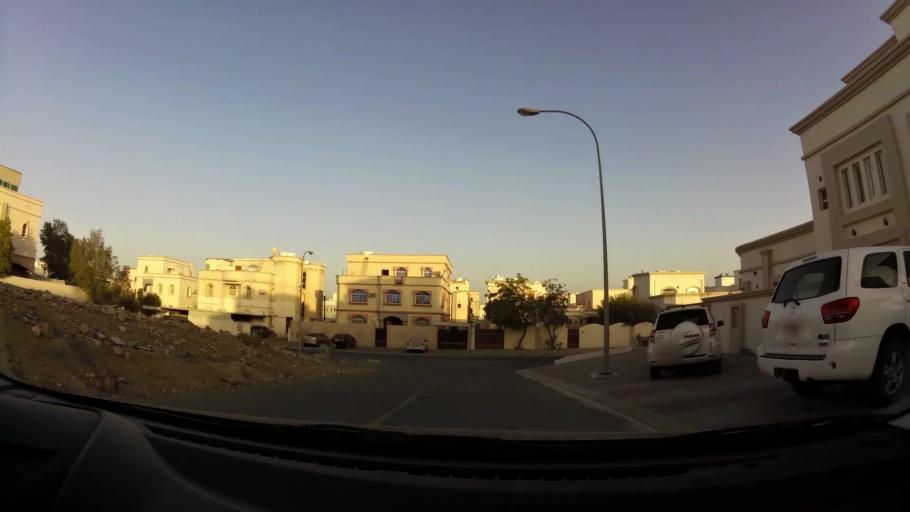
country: OM
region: Muhafazat Masqat
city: As Sib al Jadidah
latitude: 23.6009
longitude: 58.2317
